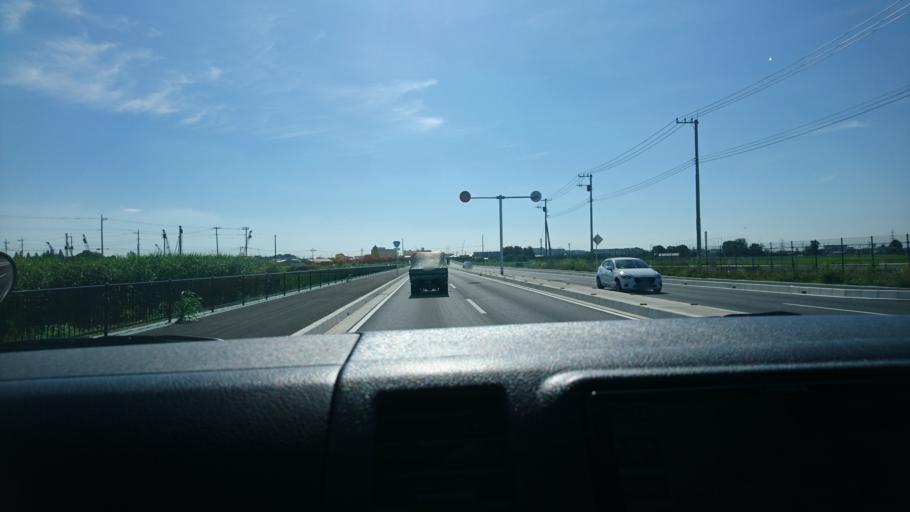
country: JP
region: Saitama
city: Kurihashi
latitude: 36.1247
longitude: 139.6516
